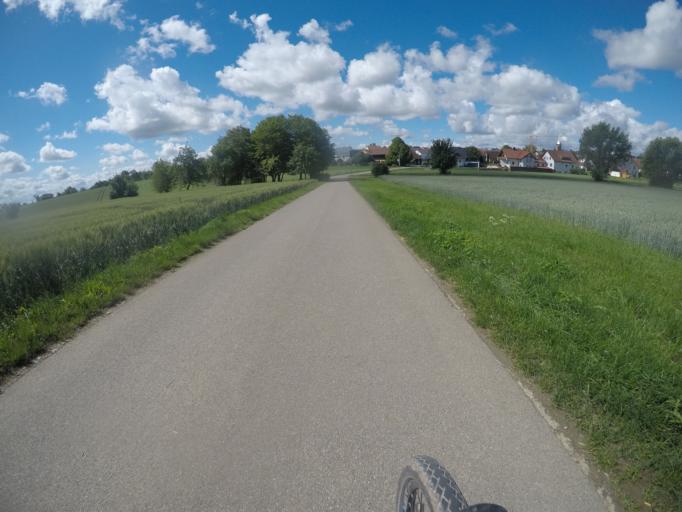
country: DE
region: Baden-Wuerttemberg
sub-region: Regierungsbezirk Stuttgart
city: Unterjettingen
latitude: 48.5692
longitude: 8.7871
